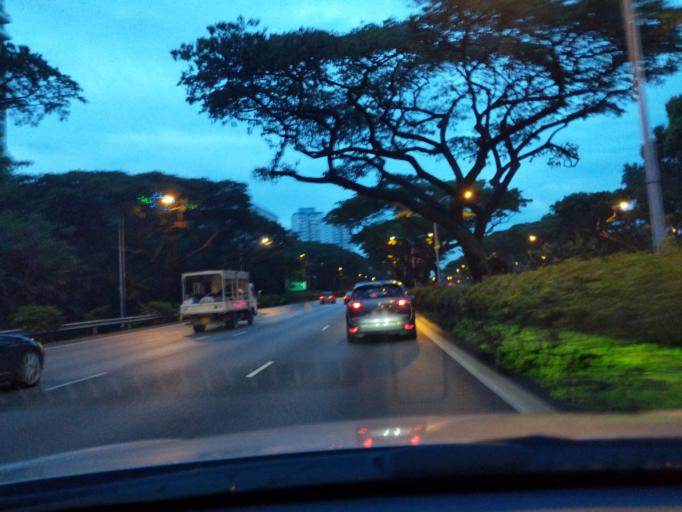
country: SG
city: Singapore
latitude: 1.2996
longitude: 103.9042
